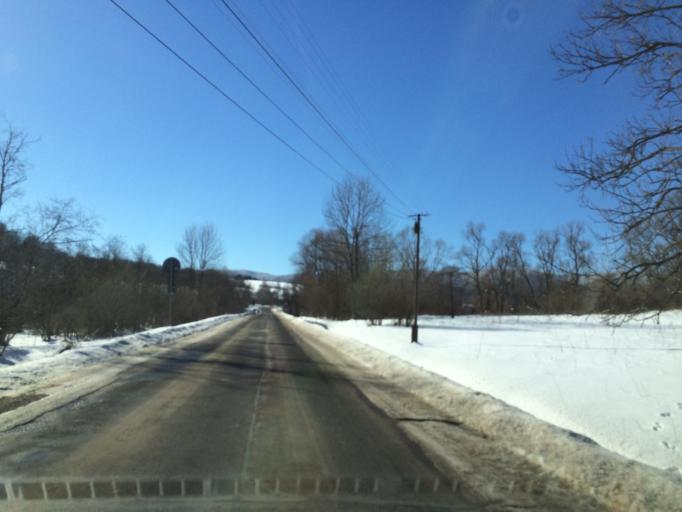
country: PL
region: Subcarpathian Voivodeship
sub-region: Powiat bieszczadzki
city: Lutowiska
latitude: 49.1143
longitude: 22.6625
